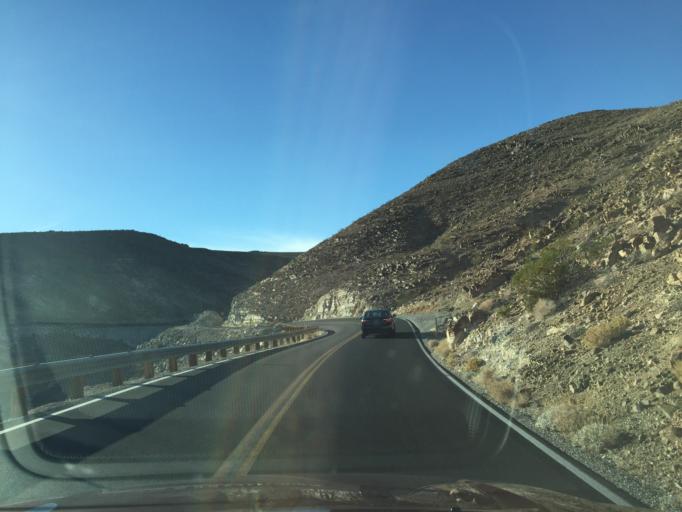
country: US
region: California
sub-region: Inyo County
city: Lone Pine
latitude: 36.3480
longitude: -117.5374
